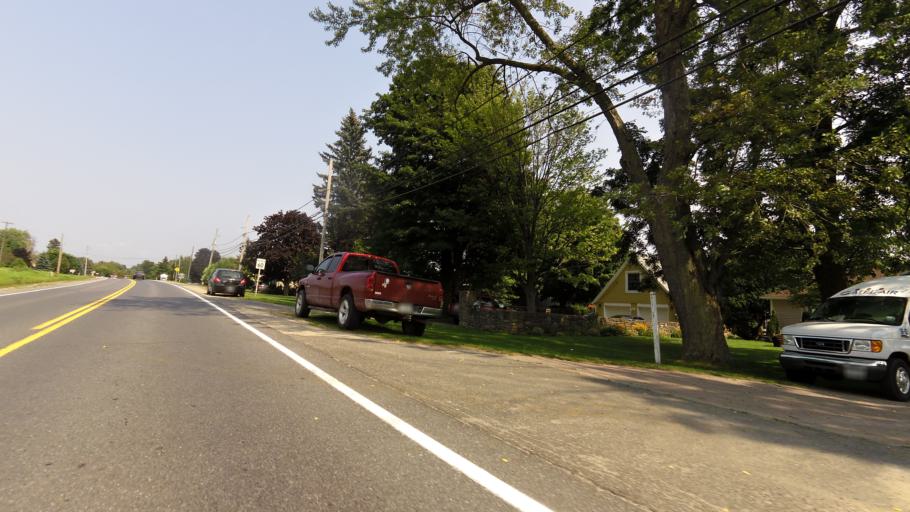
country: CA
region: Ontario
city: Prescott
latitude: 44.6962
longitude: -75.5397
